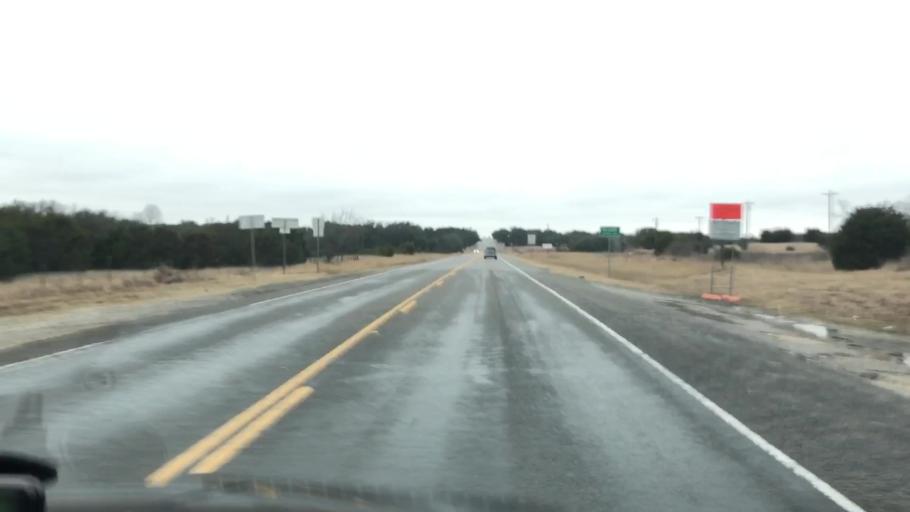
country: US
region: Texas
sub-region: Hamilton County
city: Hico
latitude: 31.9967
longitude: -98.0474
